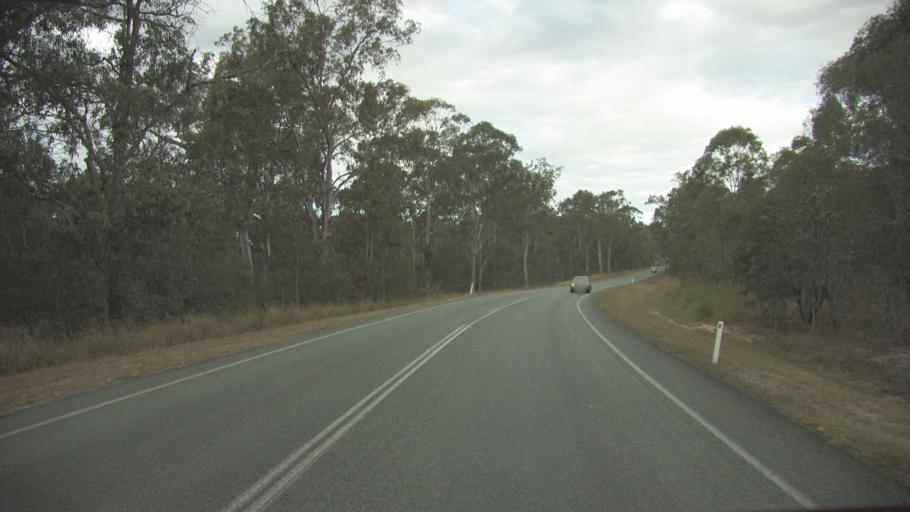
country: AU
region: Queensland
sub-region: Logan
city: Cedar Vale
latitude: -27.9020
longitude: 153.0907
